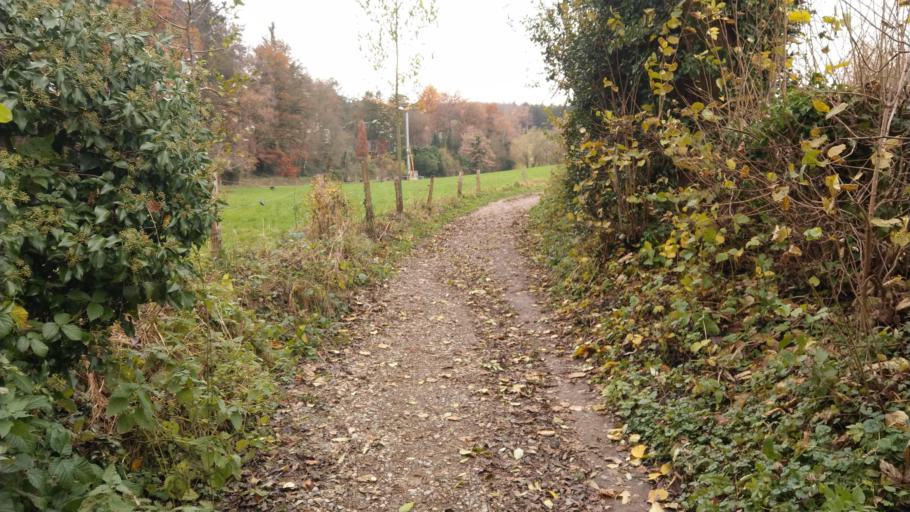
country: DE
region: North Rhine-Westphalia
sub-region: Regierungsbezirk Koln
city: Aachen
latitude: 50.7568
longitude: 6.0545
